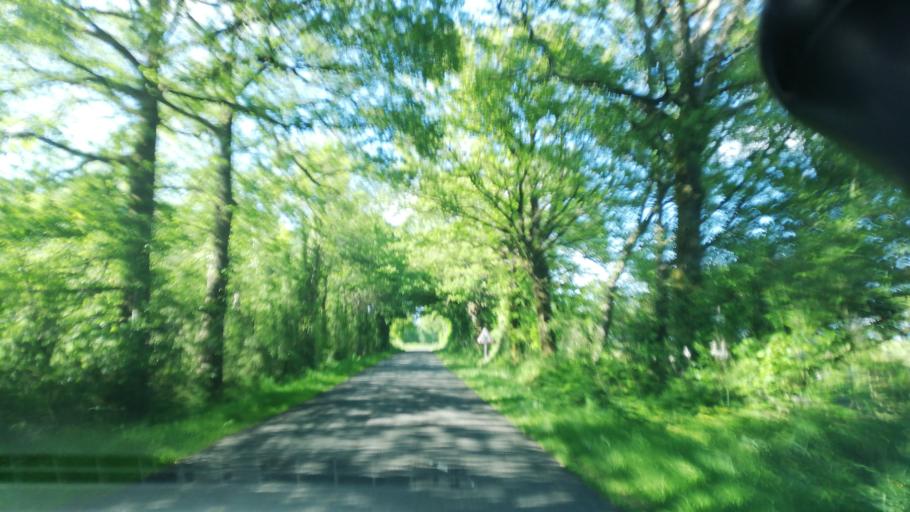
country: FR
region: Poitou-Charentes
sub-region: Departement des Deux-Sevres
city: Moncoutant
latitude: 46.6722
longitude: -0.5701
